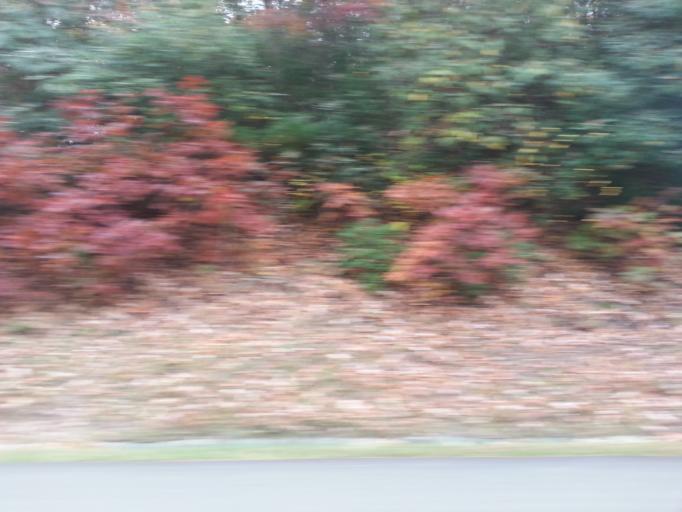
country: US
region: North Carolina
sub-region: Ashe County
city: Jefferson
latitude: 36.3150
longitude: -81.3641
